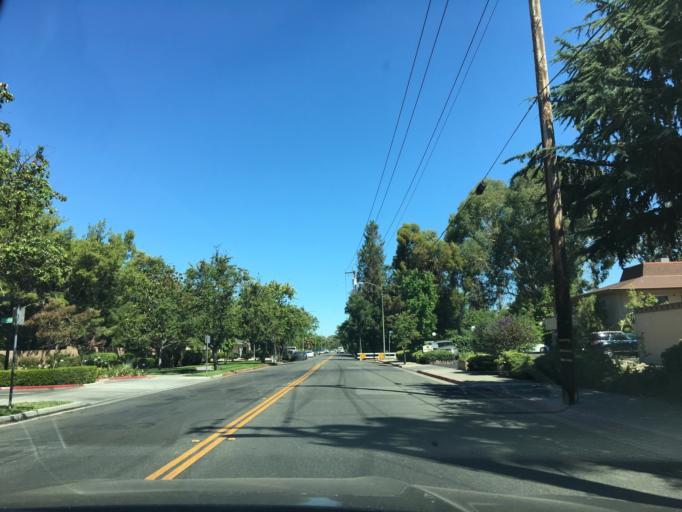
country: US
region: California
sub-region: Santa Clara County
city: East Foothills
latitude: 37.3836
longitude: -121.8281
